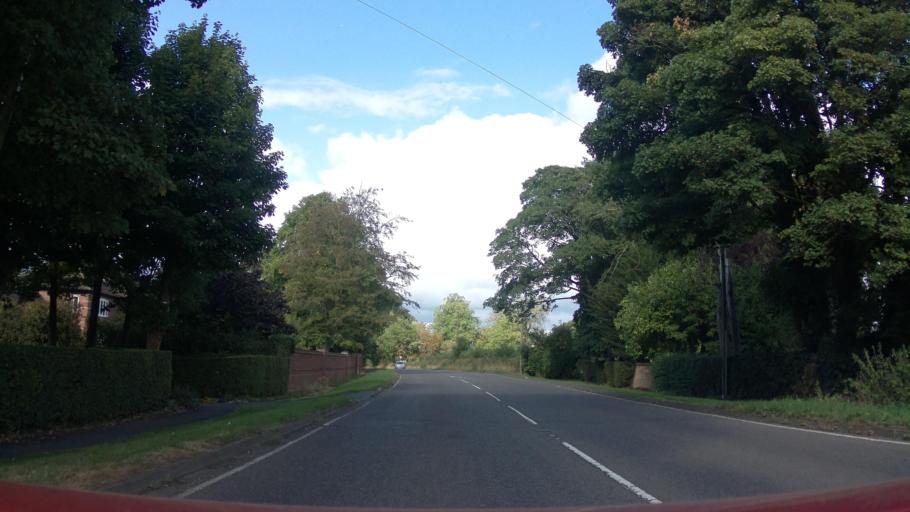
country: GB
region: England
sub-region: Leicestershire
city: Ashby de la Zouch
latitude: 52.7342
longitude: -1.4840
